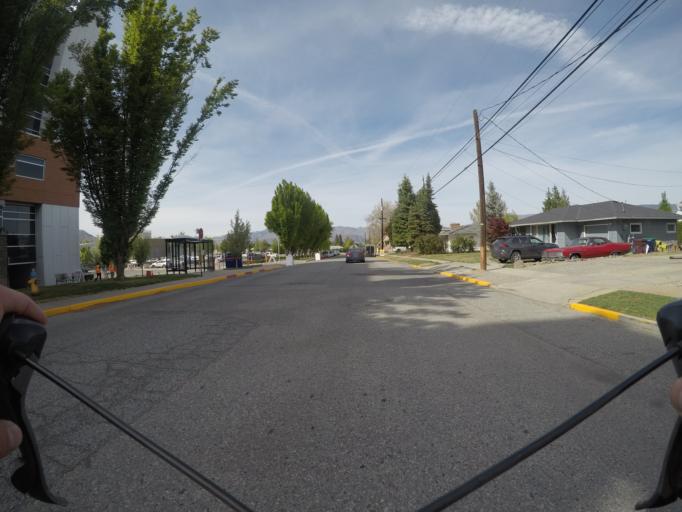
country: US
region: Washington
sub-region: Chelan County
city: Wenatchee
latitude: 47.4066
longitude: -120.3193
